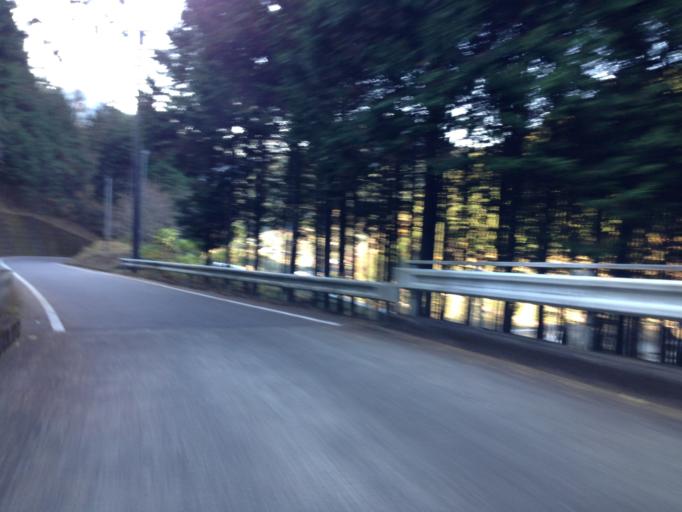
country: JP
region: Gifu
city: Mitake
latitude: 35.6092
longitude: 137.1892
